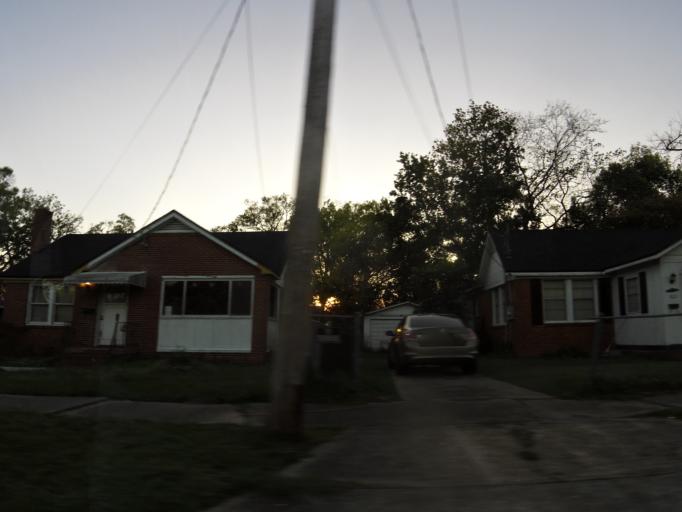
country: US
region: Florida
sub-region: Duval County
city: Jacksonville
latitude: 30.3334
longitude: -81.7166
